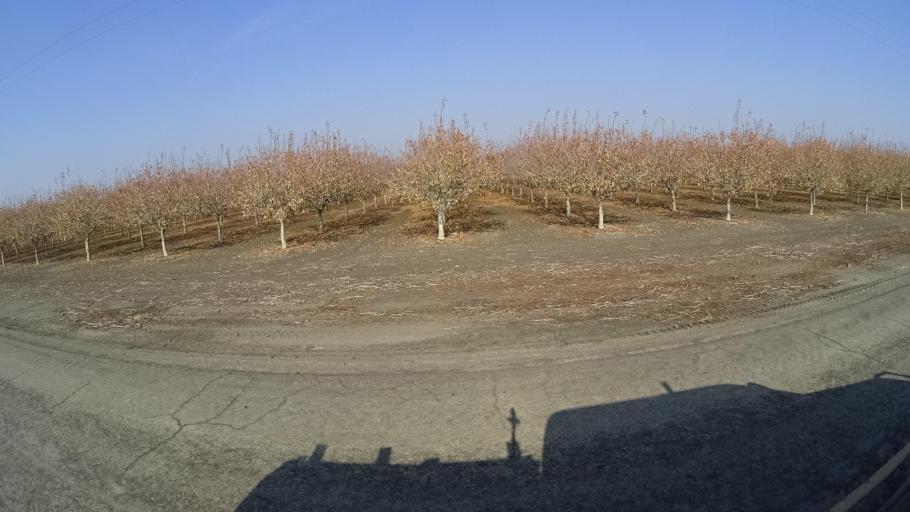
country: US
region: California
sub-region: Kern County
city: Buttonwillow
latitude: 35.3403
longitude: -119.3975
